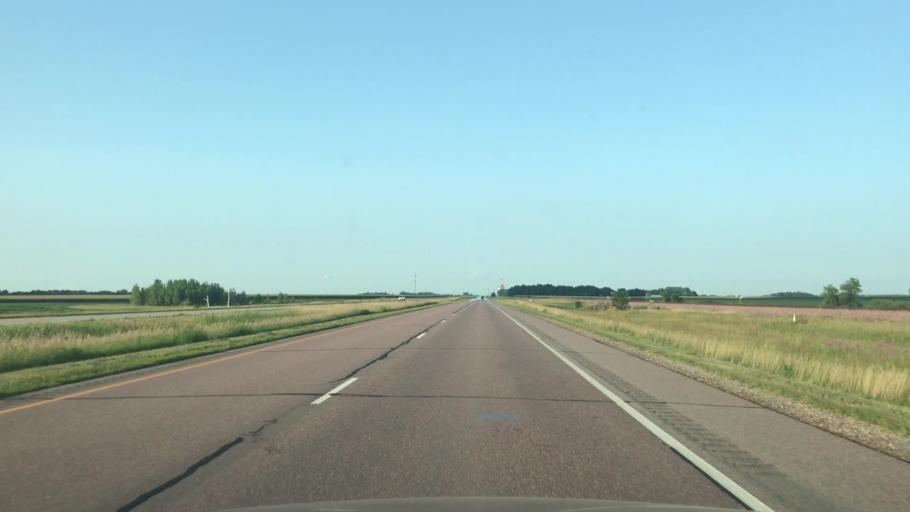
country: US
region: Minnesota
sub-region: Jackson County
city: Lakefield
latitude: 43.7504
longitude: -95.3917
